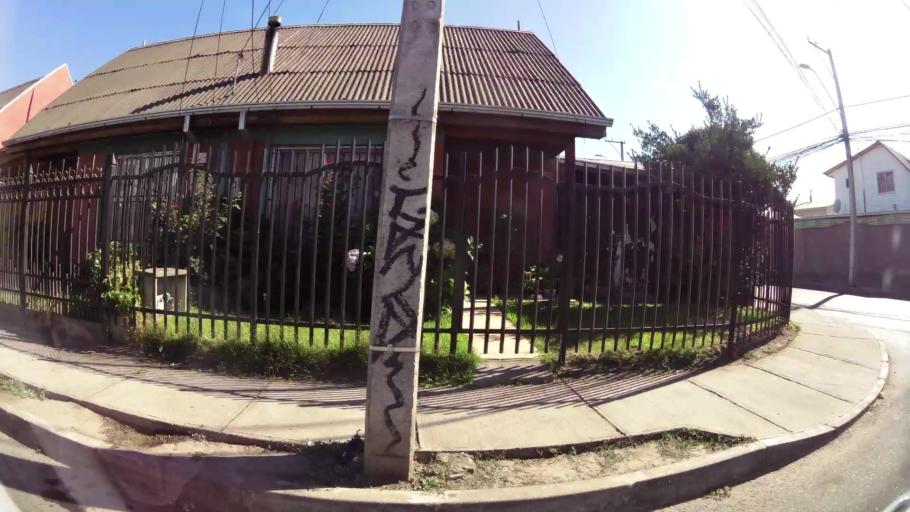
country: CL
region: Maule
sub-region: Provincia de Curico
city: Curico
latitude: -34.9809
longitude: -71.2603
